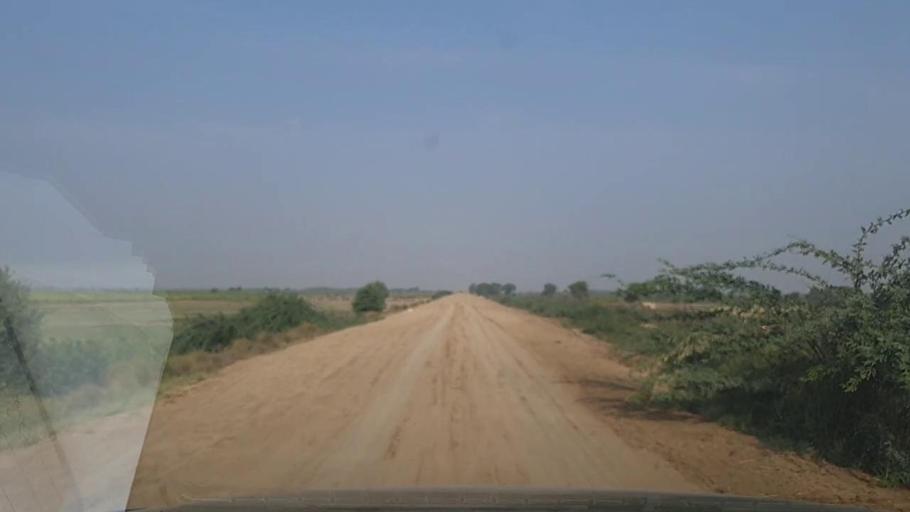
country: PK
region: Sindh
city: Bulri
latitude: 24.9929
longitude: 68.2918
